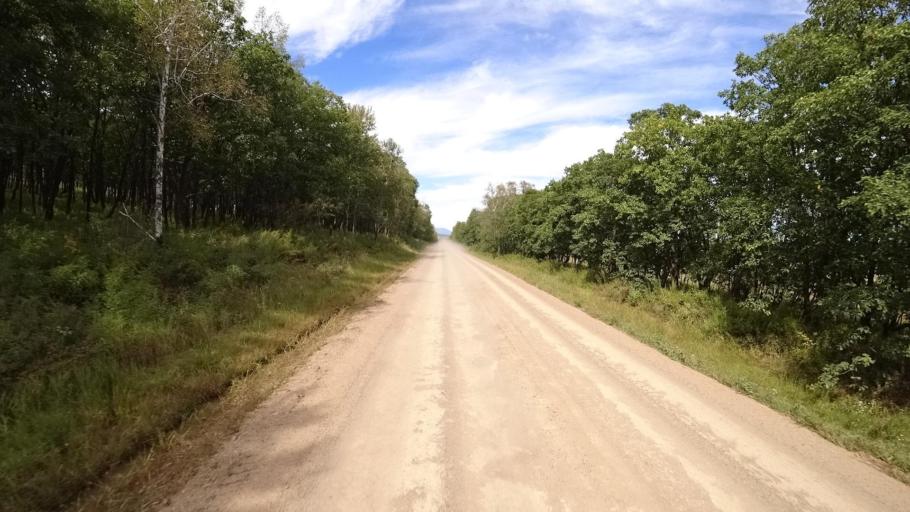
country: RU
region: Primorskiy
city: Yakovlevka
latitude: 44.6076
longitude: 133.6015
